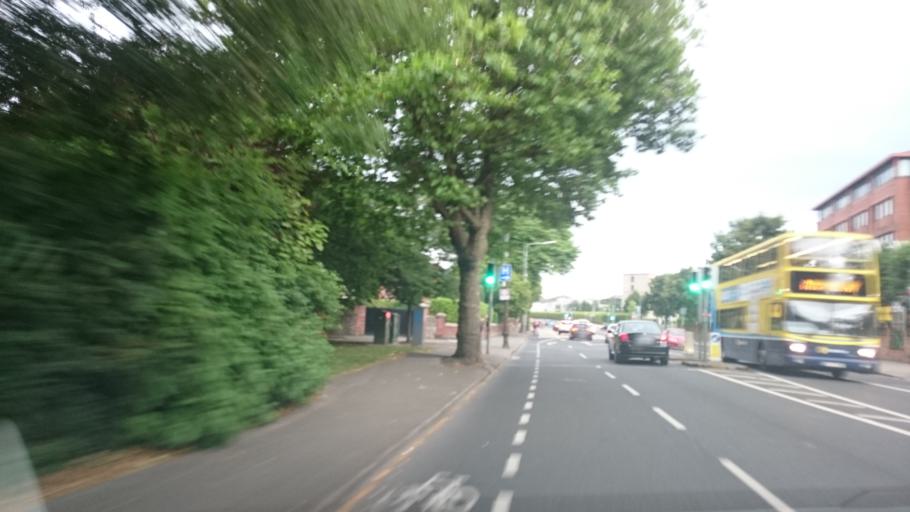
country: IE
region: Leinster
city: Donnybrook
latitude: 53.3196
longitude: -6.2139
